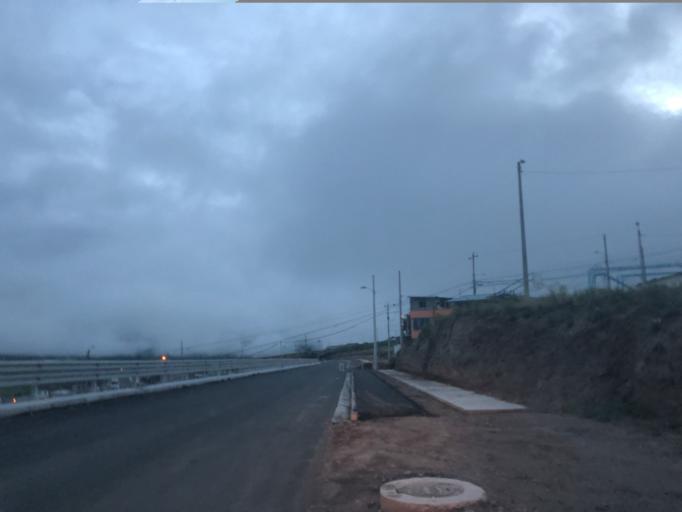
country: EC
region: Imbabura
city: Ibarra
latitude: 0.3706
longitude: -78.1304
